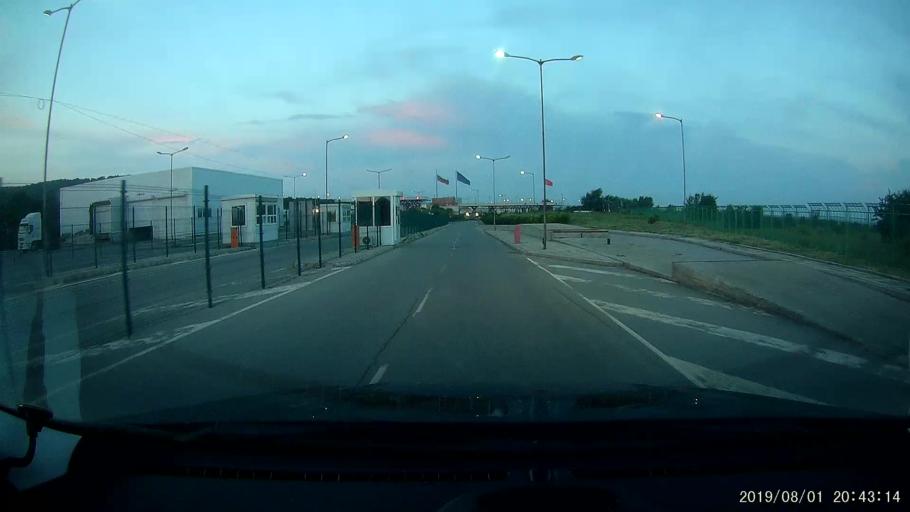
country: TR
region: Edirne
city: Lalapasa
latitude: 41.9628
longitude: 26.6021
